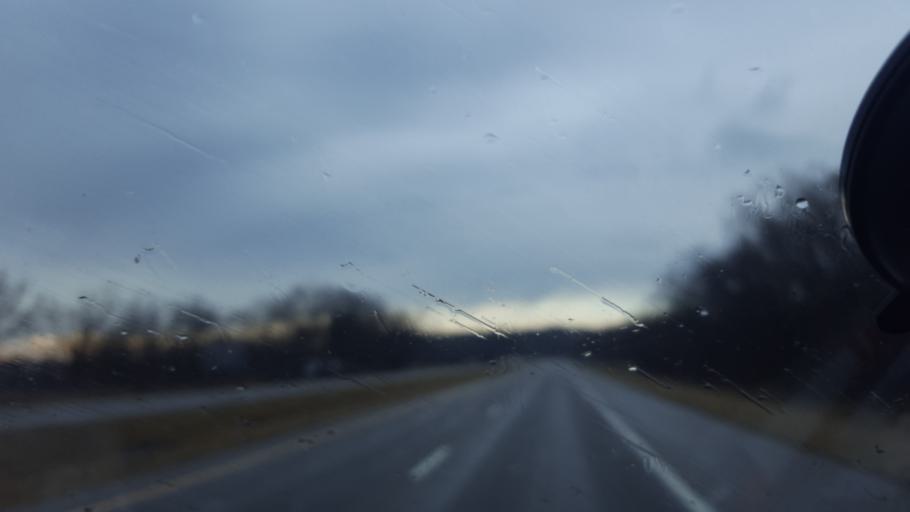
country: US
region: Ohio
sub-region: Coshocton County
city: West Lafayette
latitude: 40.2866
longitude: -81.6807
